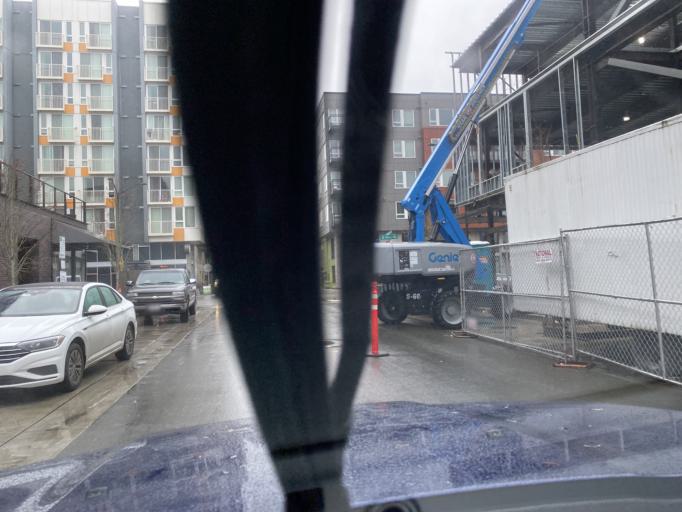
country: US
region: Washington
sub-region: King County
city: Bellevue
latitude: 47.6216
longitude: -122.1774
